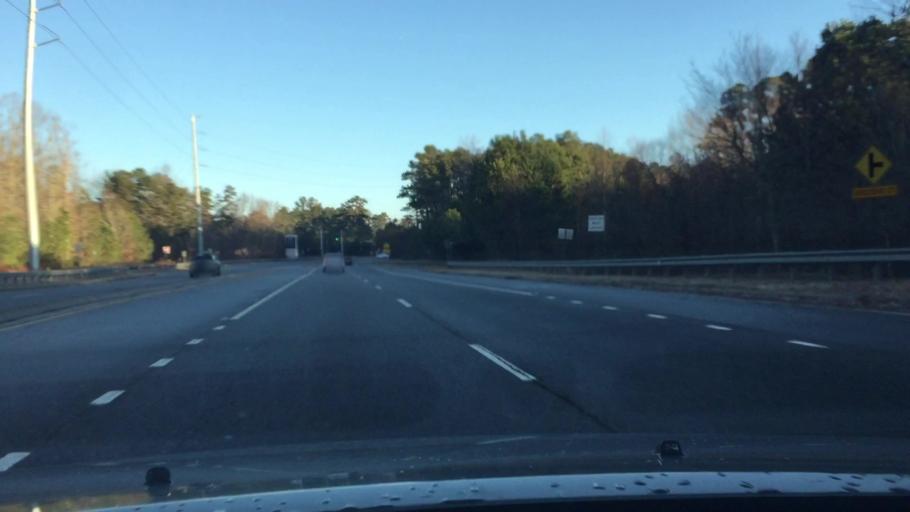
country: US
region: Georgia
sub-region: Forsyth County
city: Cumming
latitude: 34.1757
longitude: -84.1371
